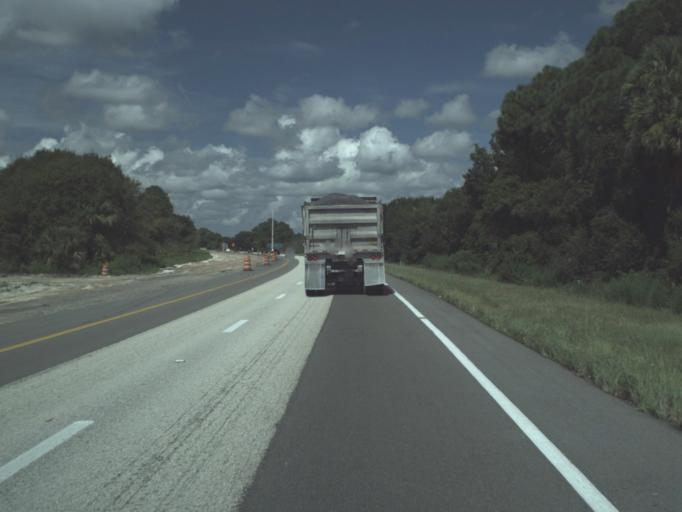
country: US
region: Florida
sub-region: Sarasota County
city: North Port
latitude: 27.0975
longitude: -82.1285
